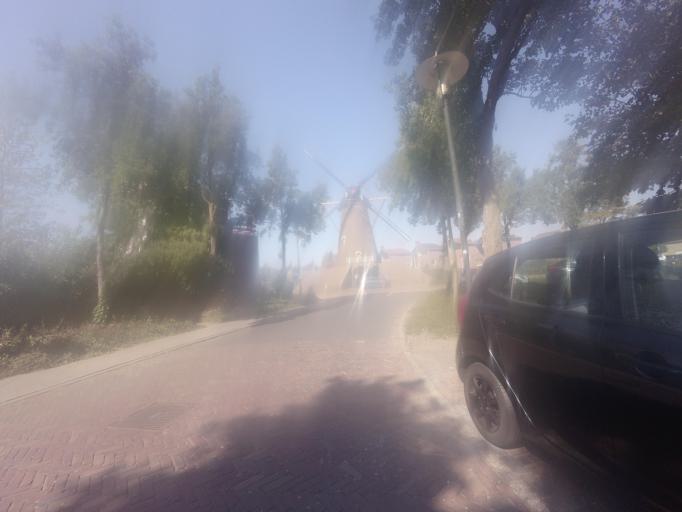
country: NL
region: North Brabant
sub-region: Gemeente Goirle
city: Goirle
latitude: 51.5204
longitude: 5.0715
